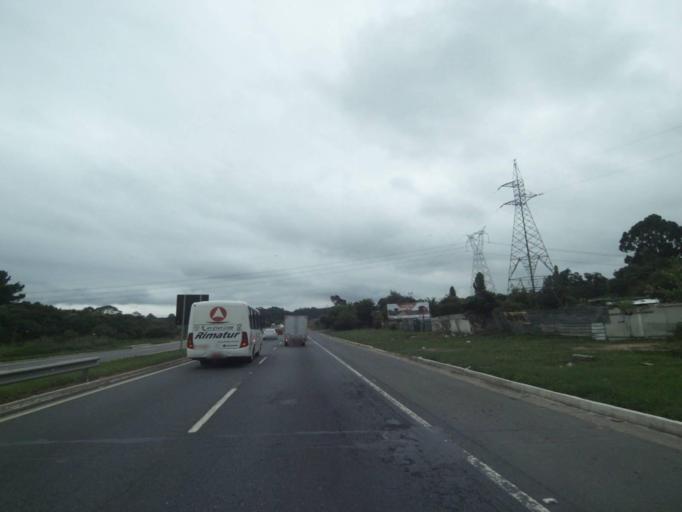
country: BR
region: Parana
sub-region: Araucaria
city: Araucaria
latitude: -25.5537
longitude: -49.3371
